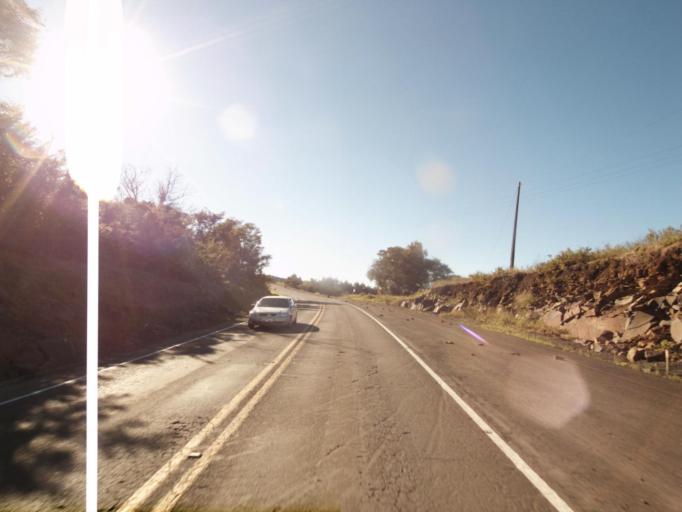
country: AR
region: Misiones
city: Bernardo de Irigoyen
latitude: -26.5621
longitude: -53.5089
